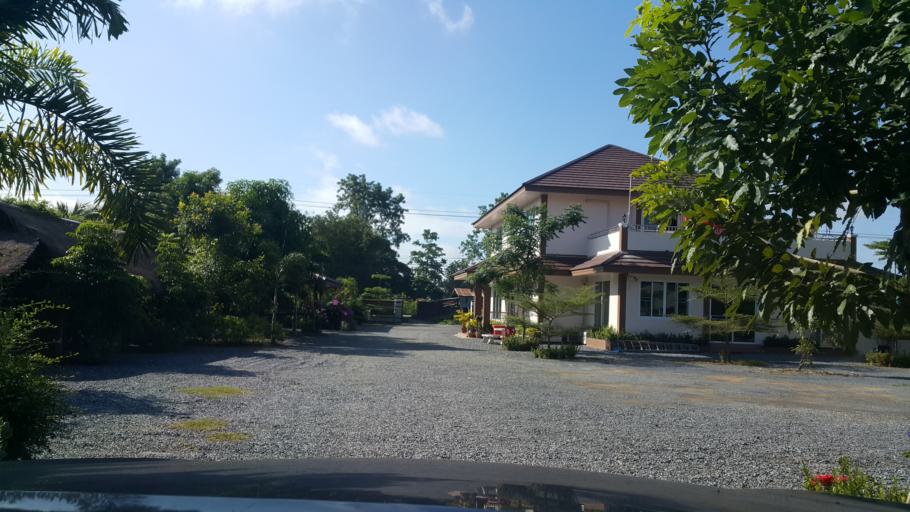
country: TH
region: Sukhothai
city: Thung Saliam
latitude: 17.3359
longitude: 99.5644
